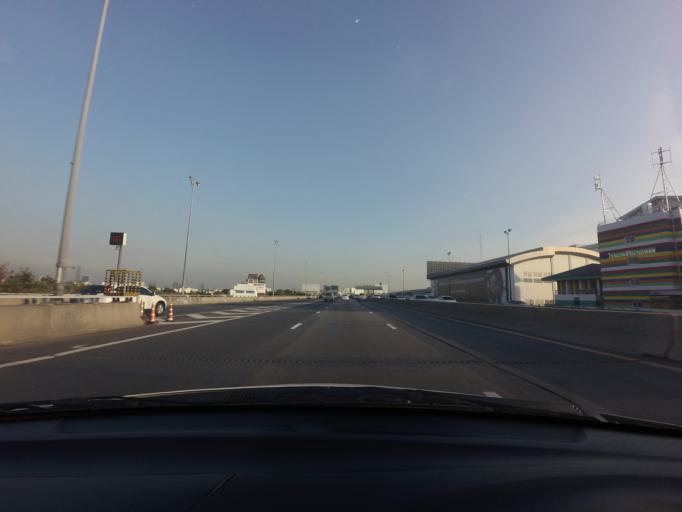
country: TH
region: Nonthaburi
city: Mueang Nonthaburi
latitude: 13.8492
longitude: 100.5333
